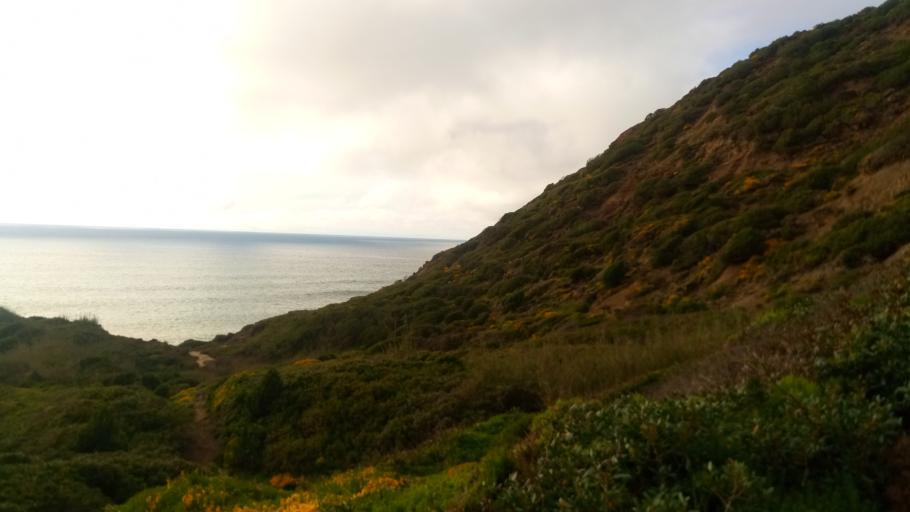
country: PT
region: Leiria
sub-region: Caldas da Rainha
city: Caldas da Rainha
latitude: 39.4968
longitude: -9.1690
